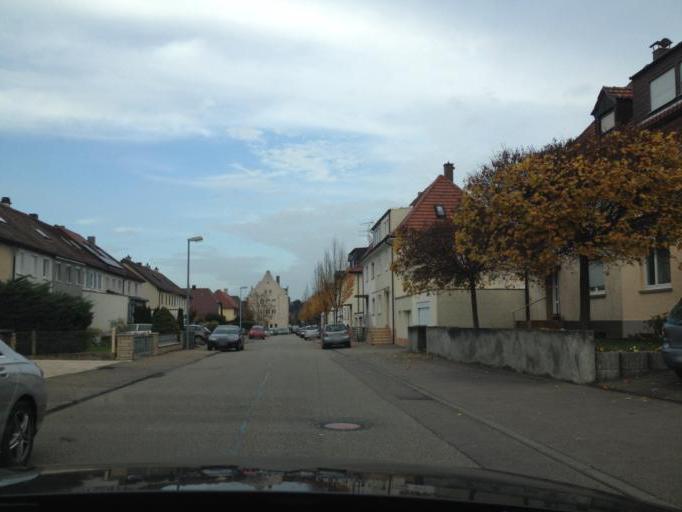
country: DE
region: Baden-Wuerttemberg
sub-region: Regierungsbezirk Stuttgart
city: Neckarsulm
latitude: 49.1977
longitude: 9.2291
